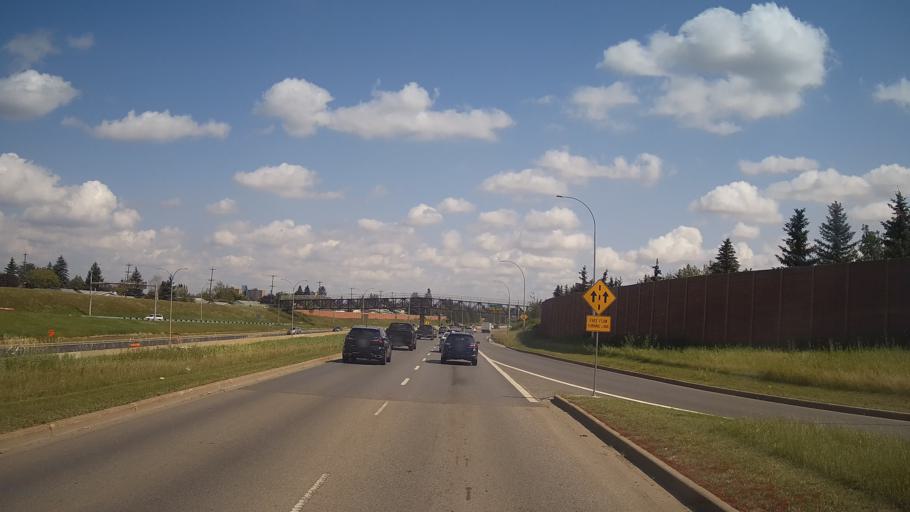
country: CA
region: Alberta
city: St. Albert
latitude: 53.5115
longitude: -113.6142
